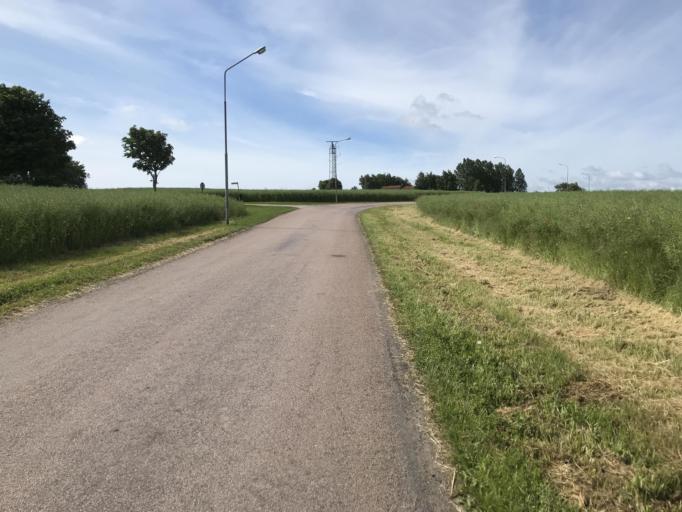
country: SE
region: Skane
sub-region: Helsingborg
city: Glumslov
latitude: 55.9358
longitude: 12.8024
